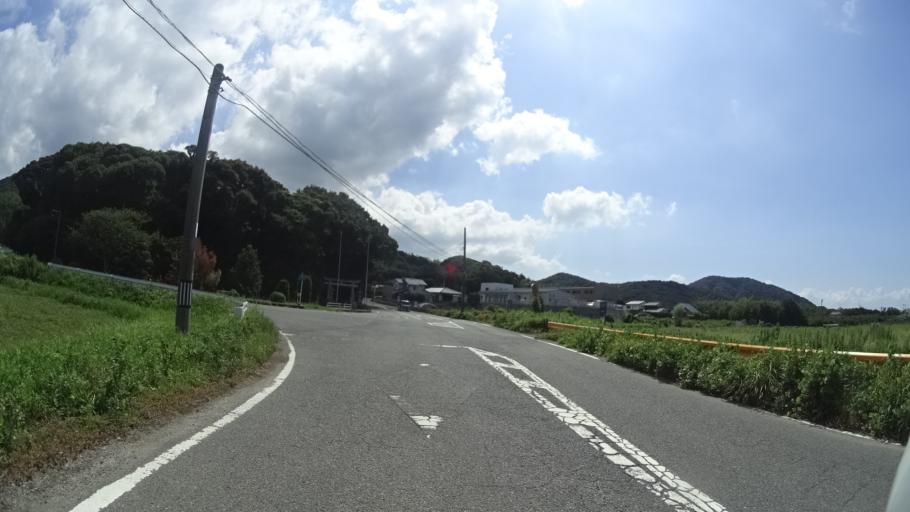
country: JP
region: Yamaguchi
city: Shimonoseki
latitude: 34.0927
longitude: 130.8813
